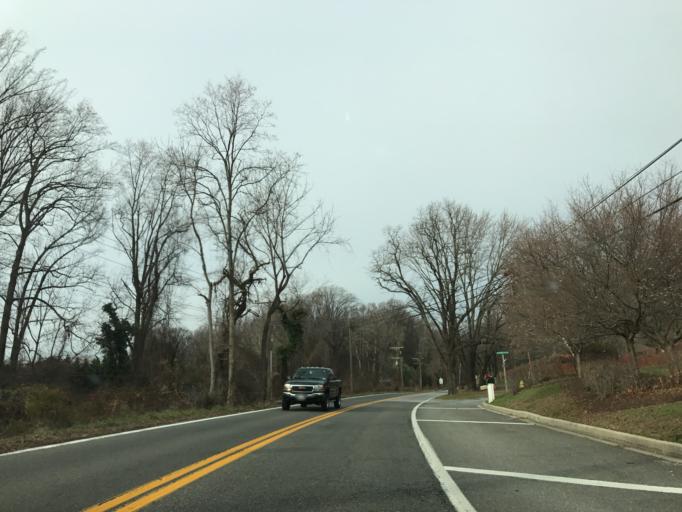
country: US
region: Maryland
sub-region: Anne Arundel County
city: Arnold
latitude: 39.0442
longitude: -76.5222
